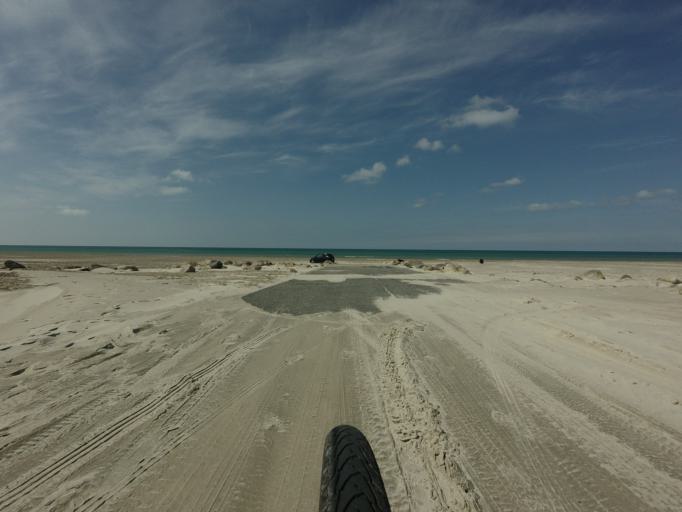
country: DK
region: North Denmark
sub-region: Jammerbugt Kommune
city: Brovst
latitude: 57.1778
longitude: 9.4369
